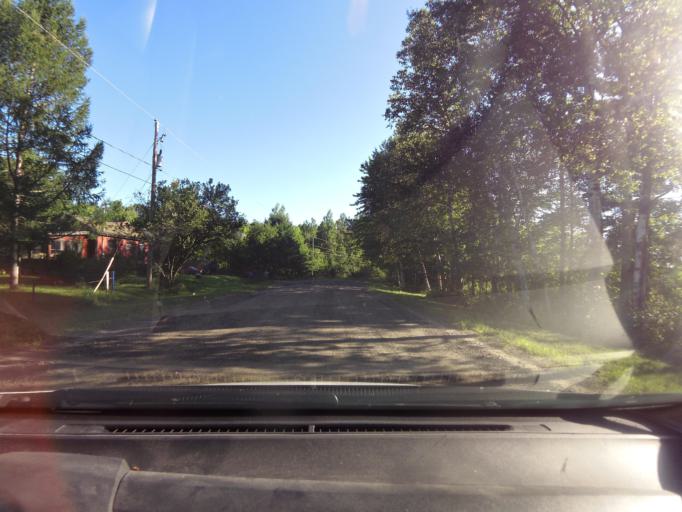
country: CA
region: Quebec
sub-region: Mauricie
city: Becancour
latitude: 46.5504
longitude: -72.3935
